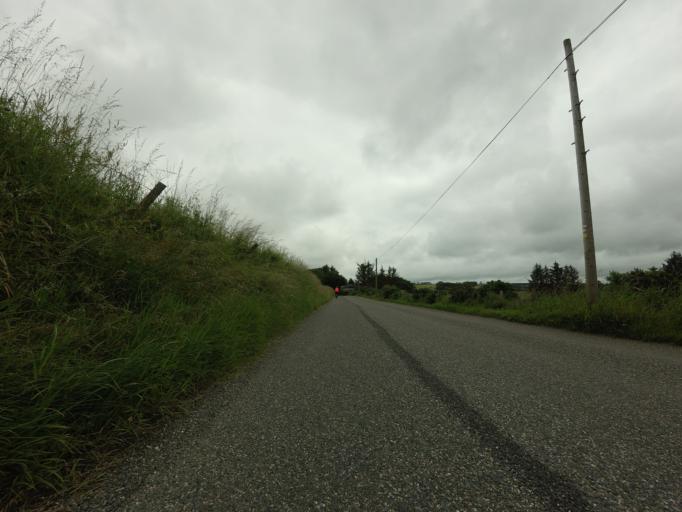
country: GB
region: Scotland
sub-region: Aberdeenshire
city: Turriff
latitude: 57.5377
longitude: -2.3716
